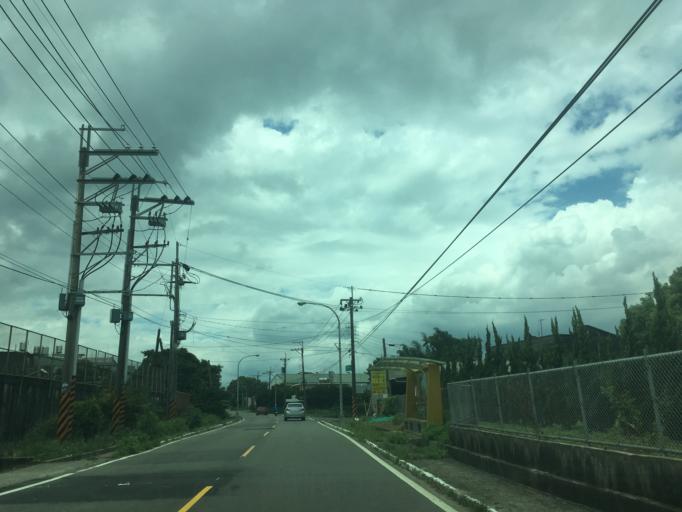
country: TW
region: Taiwan
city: Daxi
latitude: 24.8564
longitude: 121.2930
